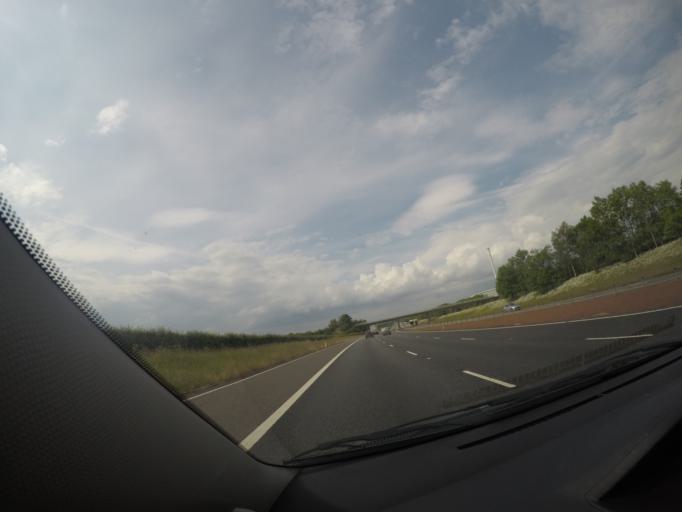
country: GB
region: Scotland
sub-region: Dumfries and Galloway
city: Lockerbie
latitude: 55.1483
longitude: -3.3817
